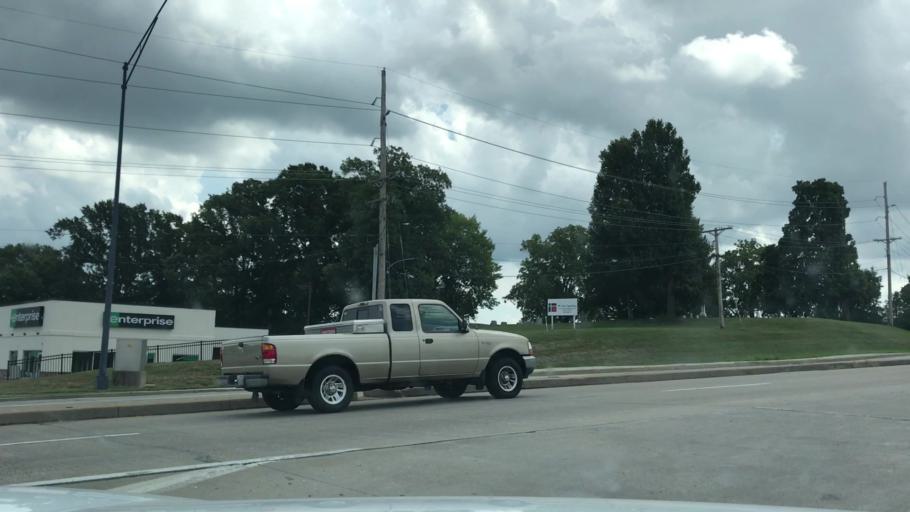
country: US
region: Missouri
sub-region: Saint Charles County
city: O'Fallon
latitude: 38.7896
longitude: -90.6997
